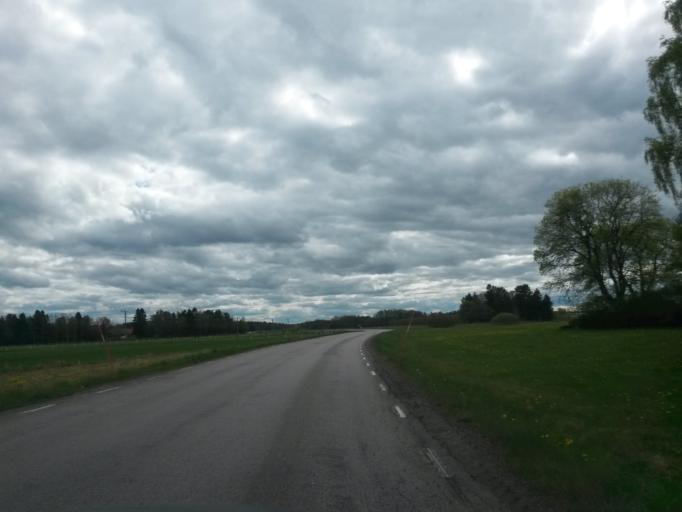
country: SE
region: Vaestra Goetaland
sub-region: Essunga Kommun
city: Nossebro
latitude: 58.2189
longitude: 12.7191
